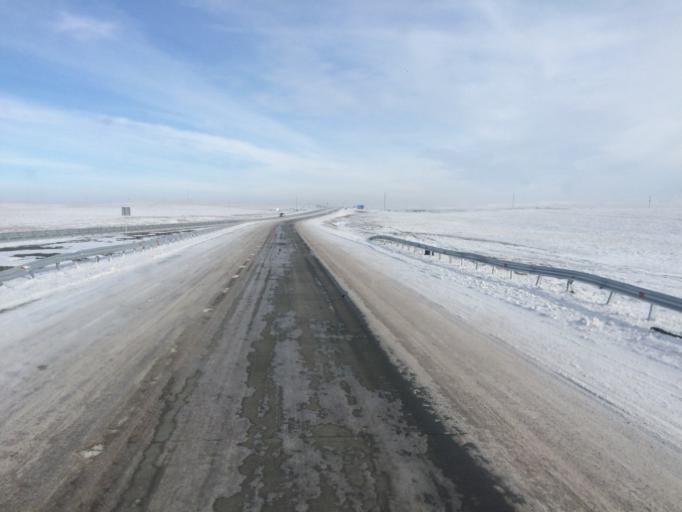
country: KZ
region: Zhambyl
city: Georgiyevka
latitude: 43.3504
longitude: 74.5480
